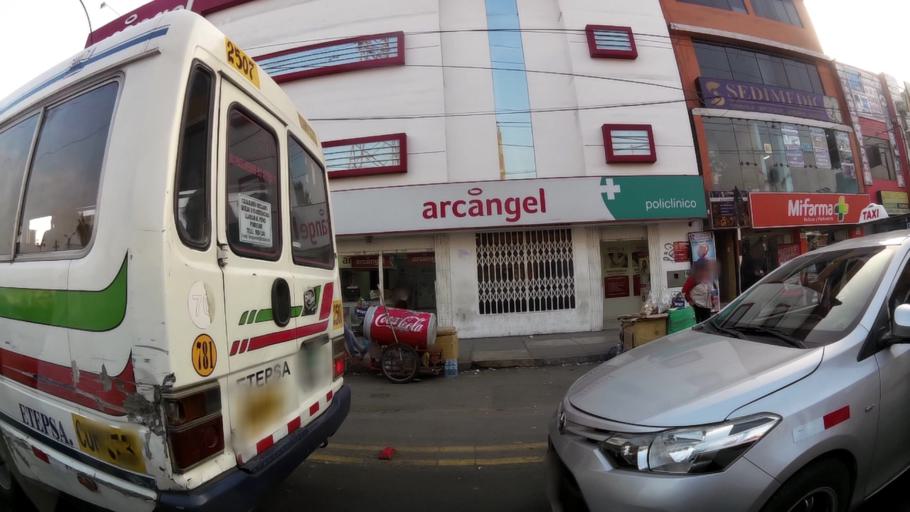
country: PE
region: Lima
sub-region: Lima
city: Independencia
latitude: -11.9908
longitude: -77.0718
